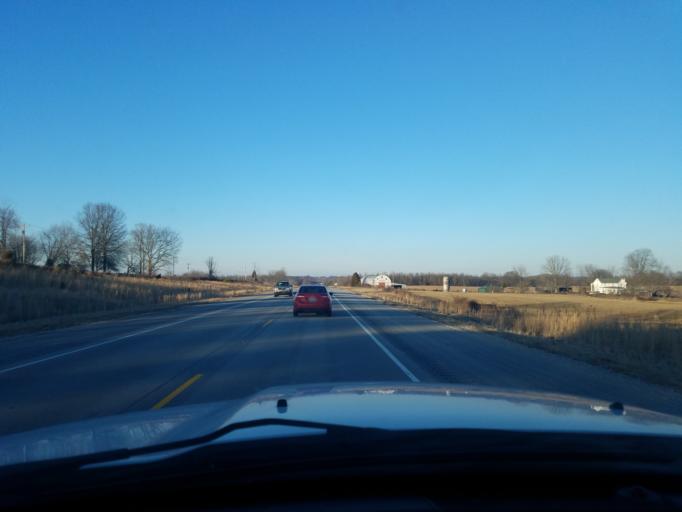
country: US
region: Indiana
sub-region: Crawford County
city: English
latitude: 38.2125
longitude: -86.5936
